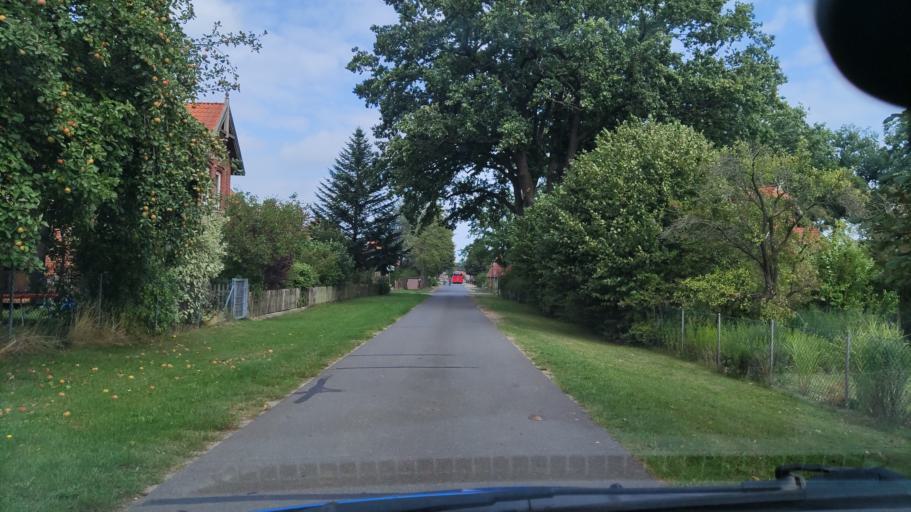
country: DE
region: Lower Saxony
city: Jelmstorf
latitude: 53.1441
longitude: 10.5315
